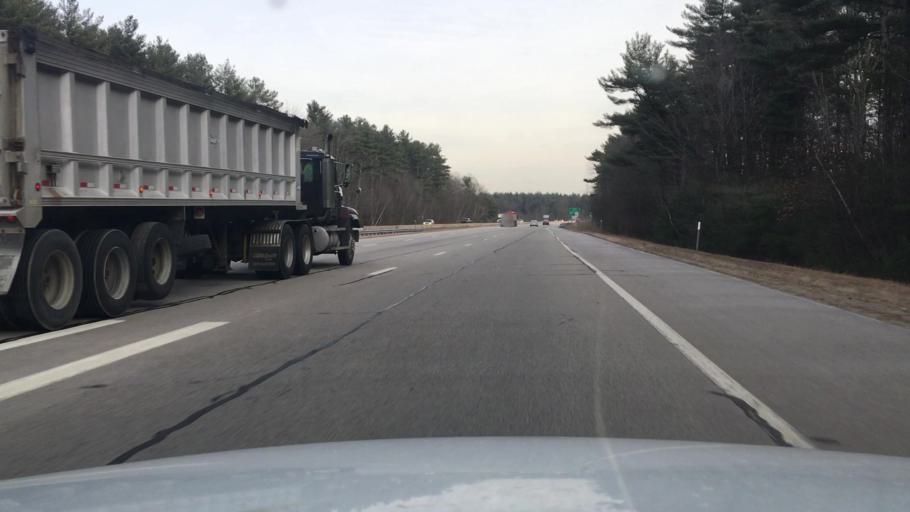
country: US
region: New Hampshire
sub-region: Rockingham County
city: Epping
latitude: 43.0254
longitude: -71.0685
